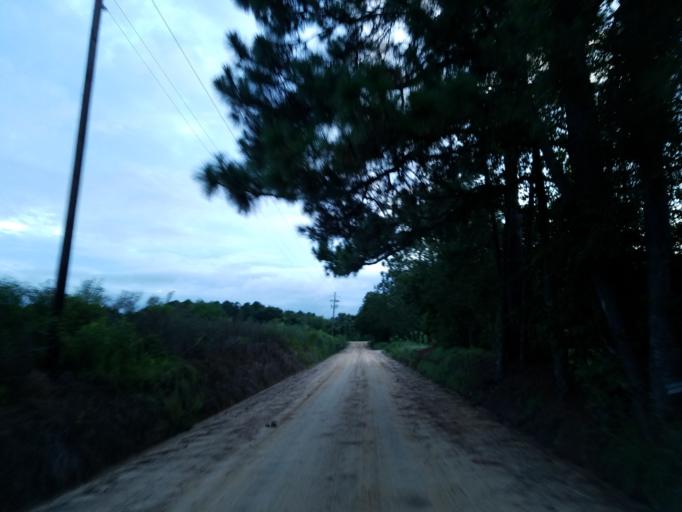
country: US
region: Georgia
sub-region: Tift County
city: Tifton
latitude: 31.5309
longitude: -83.5299
